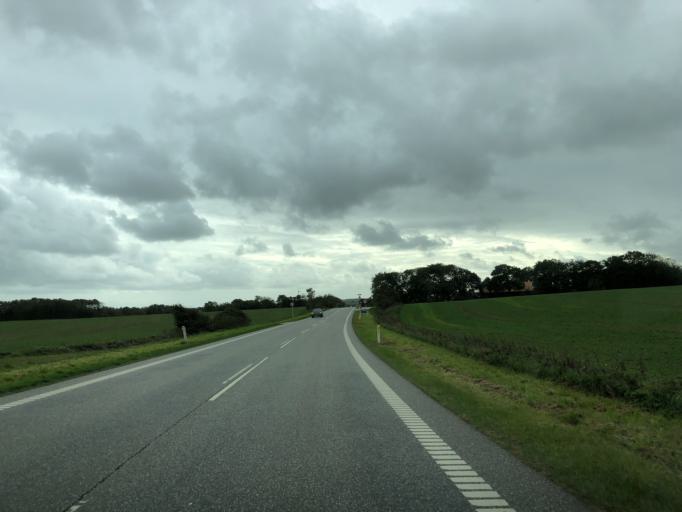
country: DK
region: North Denmark
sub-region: Thisted Kommune
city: Hurup
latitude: 56.7973
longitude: 8.4717
